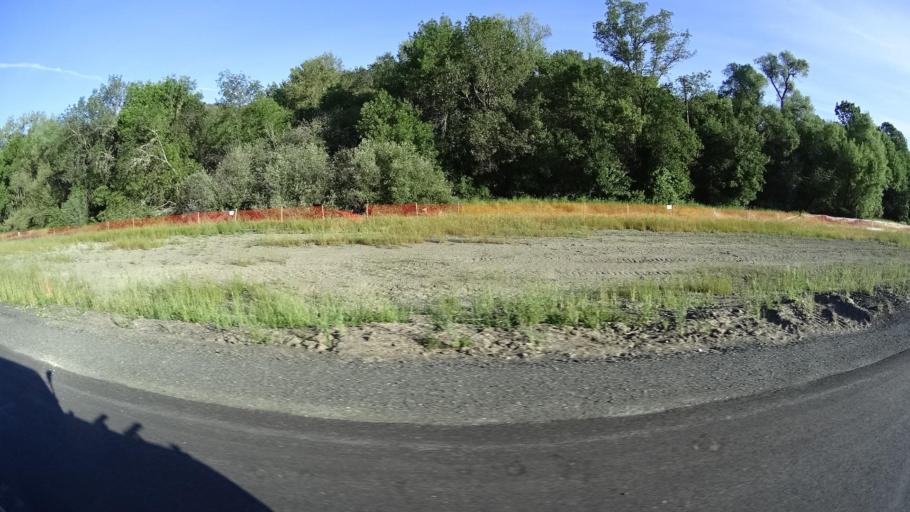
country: US
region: California
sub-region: Lake County
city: Upper Lake
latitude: 39.1678
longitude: -122.9613
